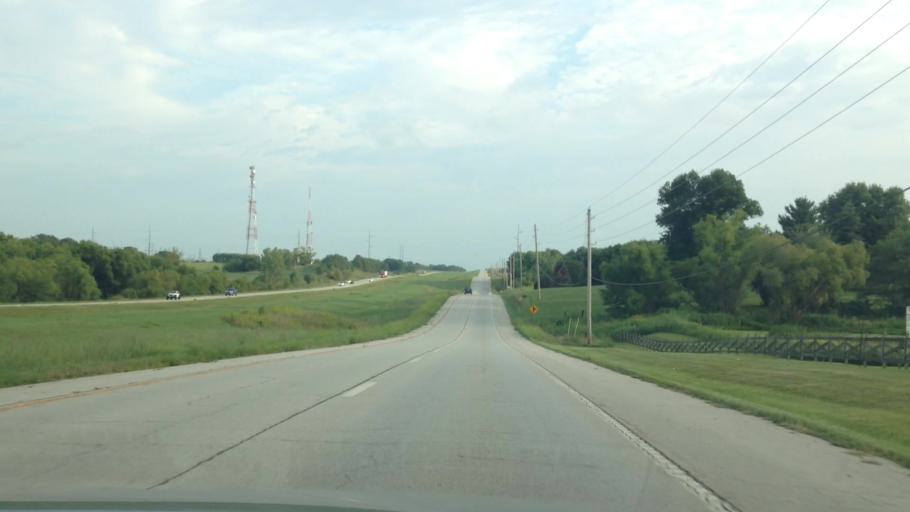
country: US
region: Missouri
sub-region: Clay County
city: Smithville
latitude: 39.3395
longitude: -94.5843
